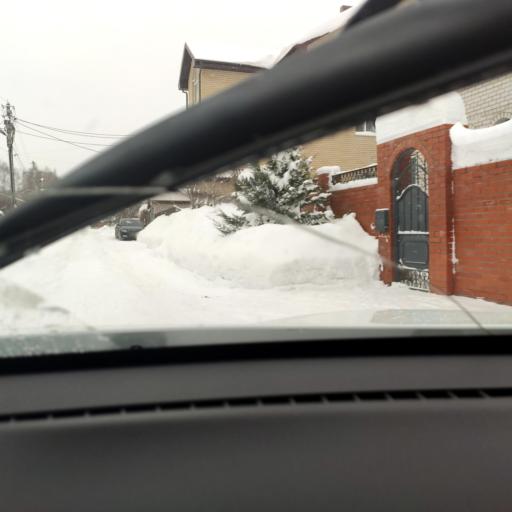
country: RU
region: Tatarstan
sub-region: Gorod Kazan'
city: Kazan
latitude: 55.7264
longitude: 49.1638
